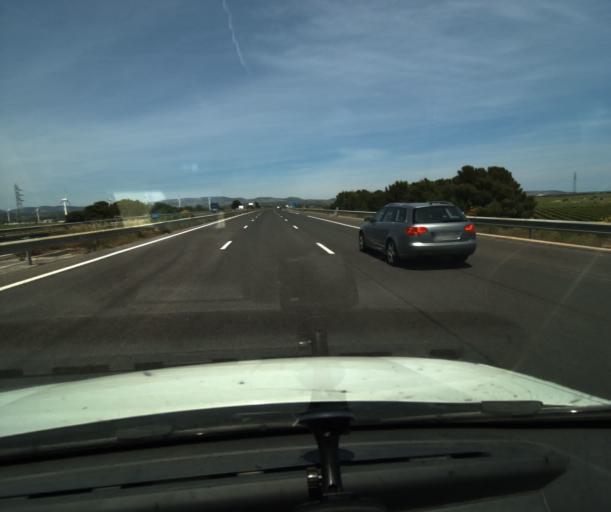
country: FR
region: Languedoc-Roussillon
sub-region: Departement des Pyrenees-Orientales
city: Rivesaltes
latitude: 42.7906
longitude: 2.8955
